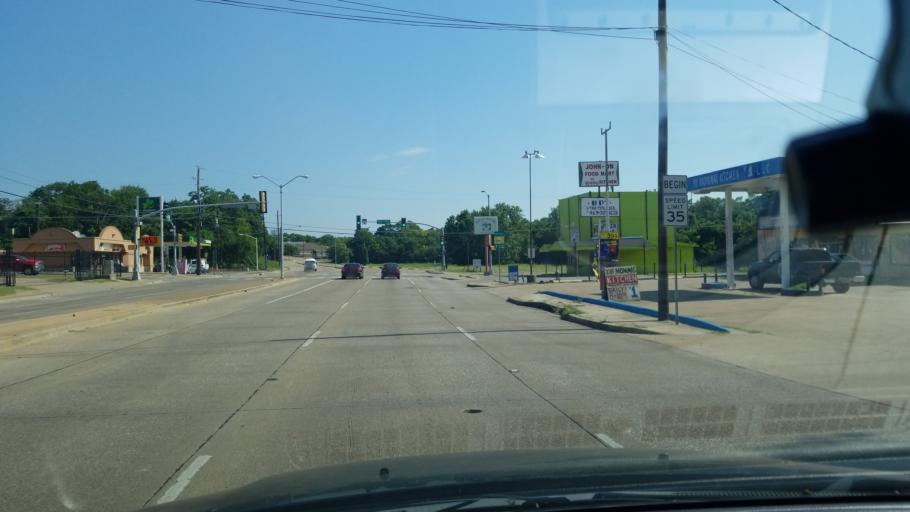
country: US
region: Texas
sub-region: Dallas County
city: Dallas
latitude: 32.7383
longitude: -96.7987
